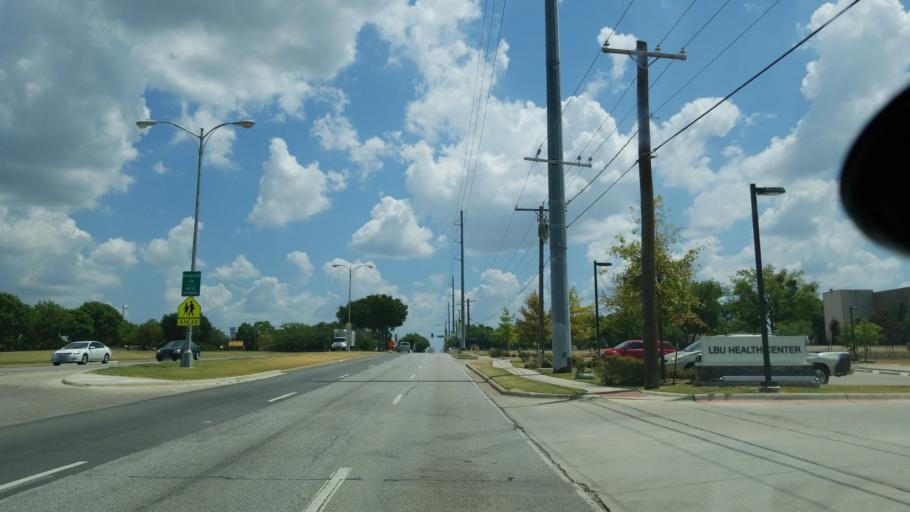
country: US
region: Texas
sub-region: Dallas County
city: Cockrell Hill
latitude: 32.7204
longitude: -96.9023
